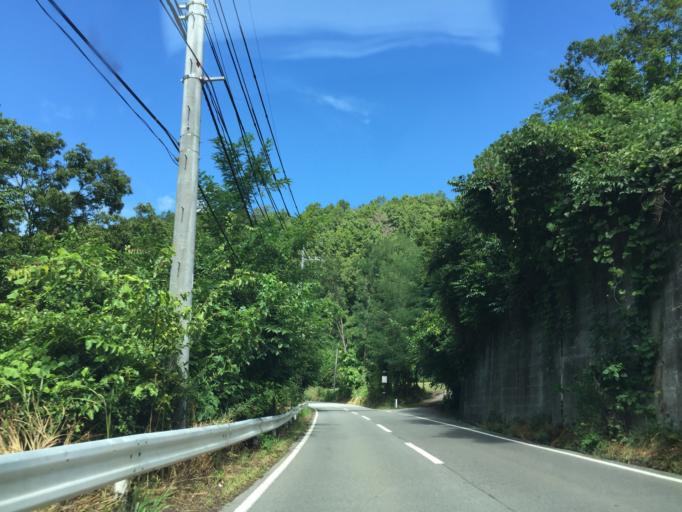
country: JP
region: Yamanashi
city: Nirasaki
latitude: 35.7874
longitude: 138.4096
